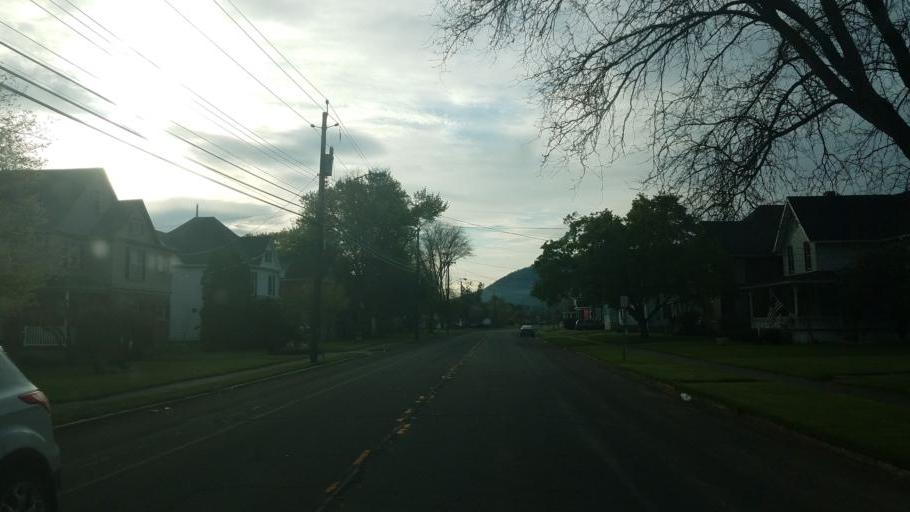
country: US
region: New York
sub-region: Steuben County
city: Canisteo
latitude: 42.2687
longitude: -77.6004
